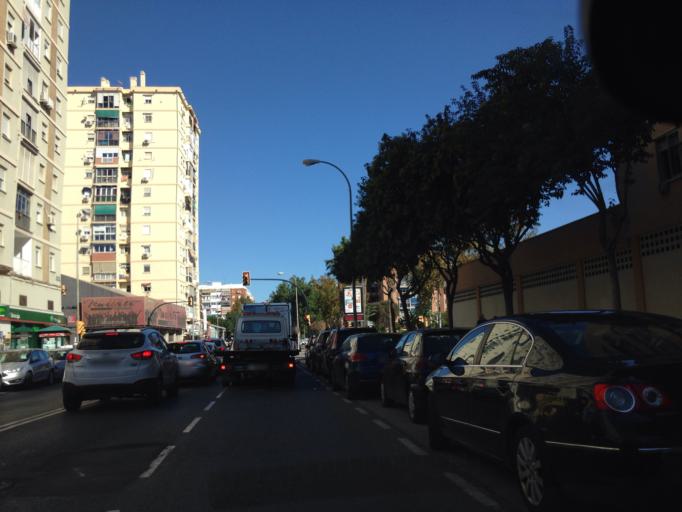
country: ES
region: Andalusia
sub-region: Provincia de Malaga
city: Malaga
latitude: 36.6913
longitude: -4.4502
